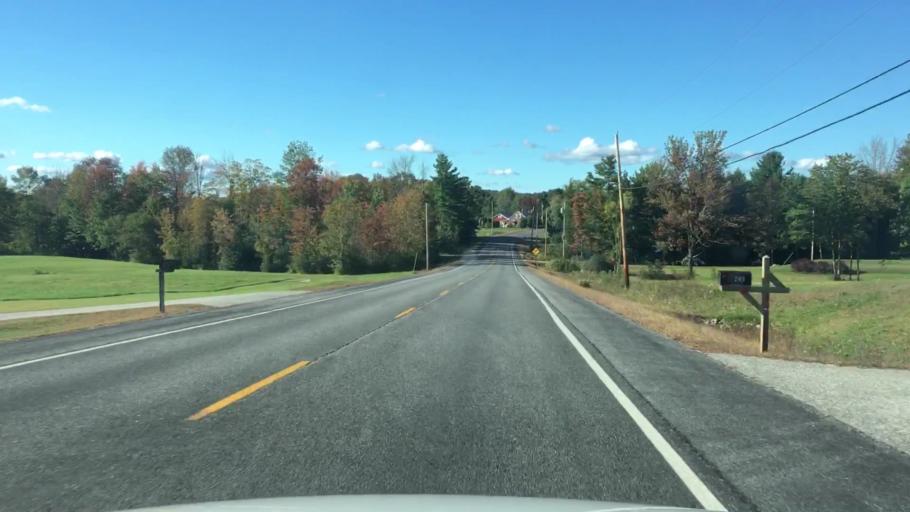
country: US
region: Maine
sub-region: Androscoggin County
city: Lisbon
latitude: 44.0399
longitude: -70.0749
